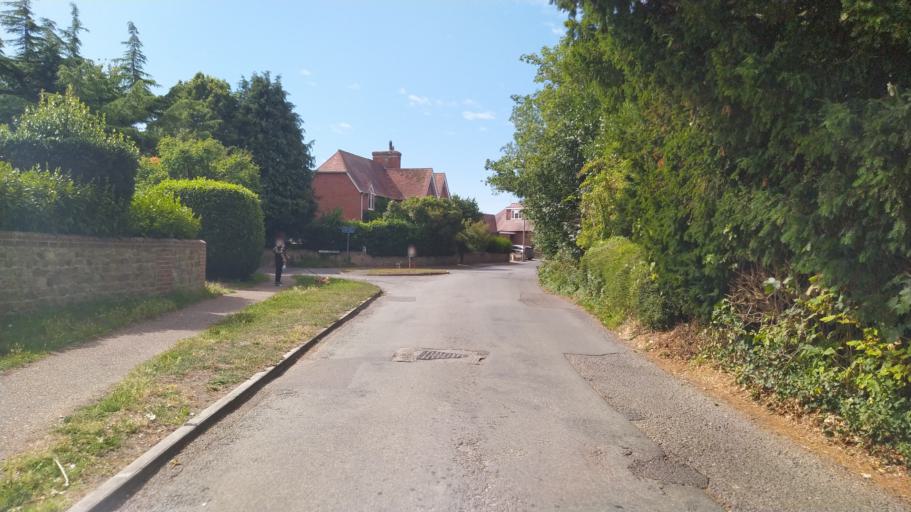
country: GB
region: England
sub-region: West Sussex
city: Chichester
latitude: 50.8129
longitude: -0.7588
